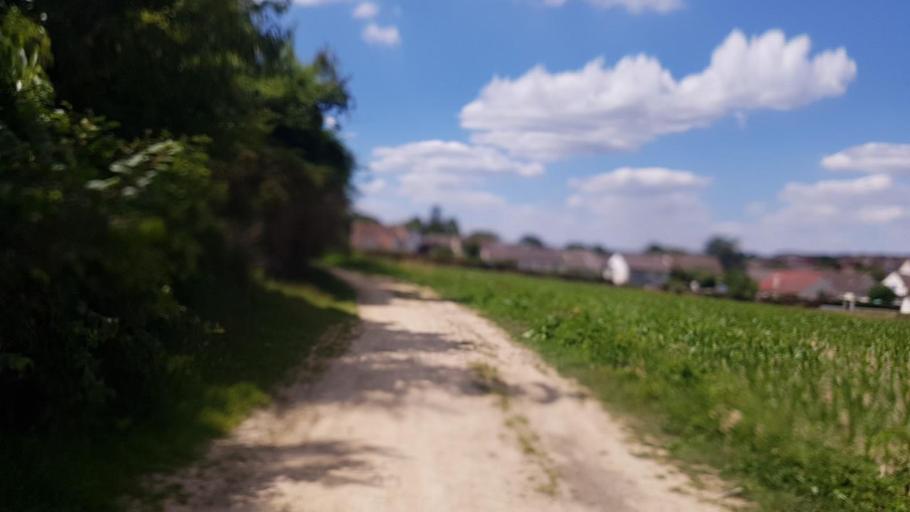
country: FR
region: Ile-de-France
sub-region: Departement de Seine-et-Marne
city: Moussy-le-Vieux
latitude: 49.0432
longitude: 2.6295
